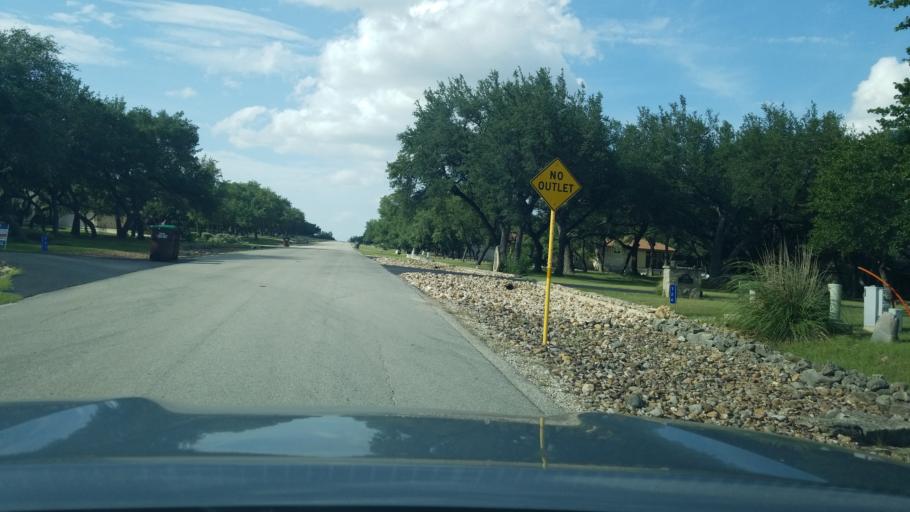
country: US
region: Texas
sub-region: Comal County
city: Bulverde
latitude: 29.8077
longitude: -98.3977
